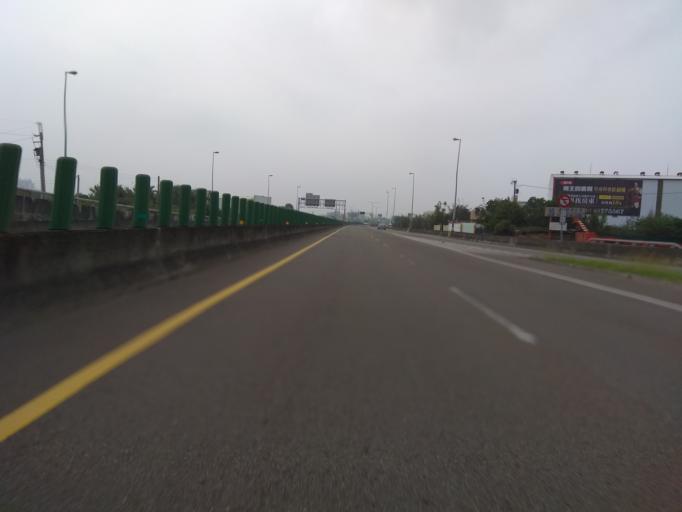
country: TW
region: Taiwan
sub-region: Miaoli
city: Miaoli
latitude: 24.7006
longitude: 120.8660
